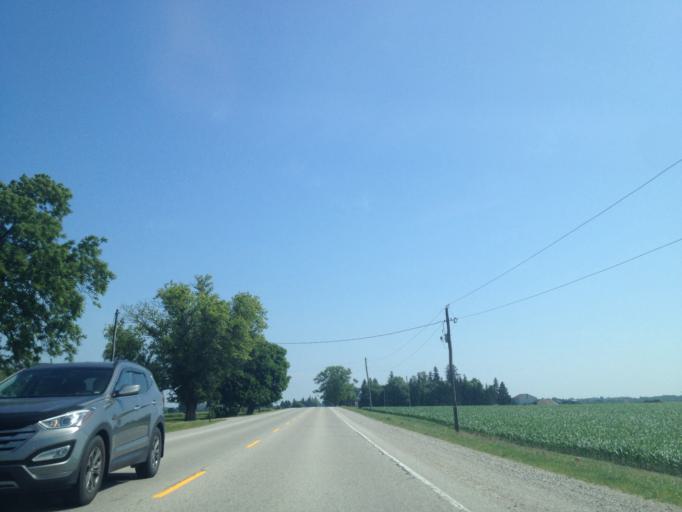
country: CA
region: Ontario
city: London
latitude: 43.2338
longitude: -81.2257
